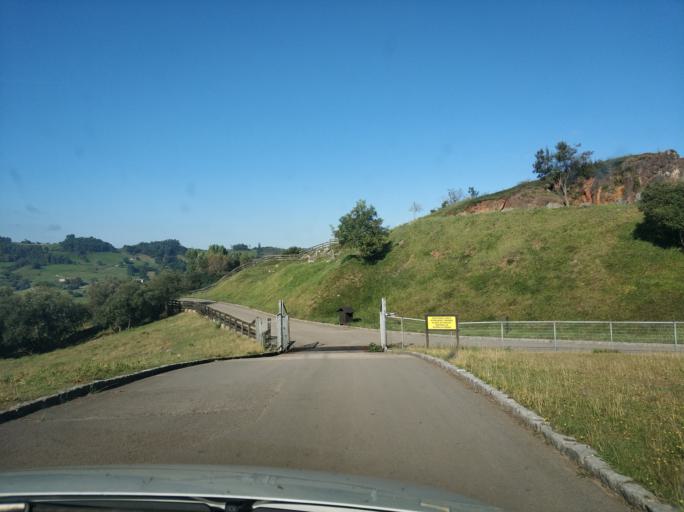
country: ES
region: Cantabria
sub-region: Provincia de Cantabria
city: Santa Maria de Cayon
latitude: 43.3440
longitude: -3.8520
